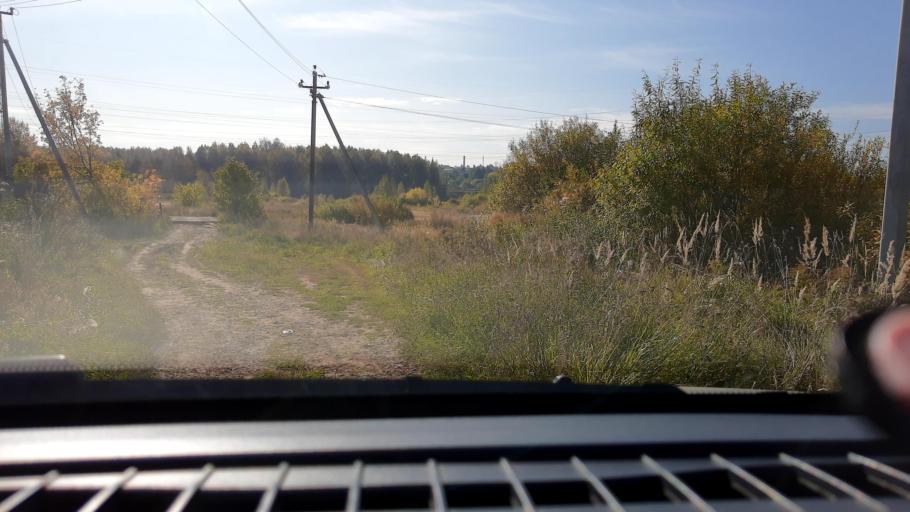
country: RU
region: Nizjnij Novgorod
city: Afonino
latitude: 56.2380
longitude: 44.0595
